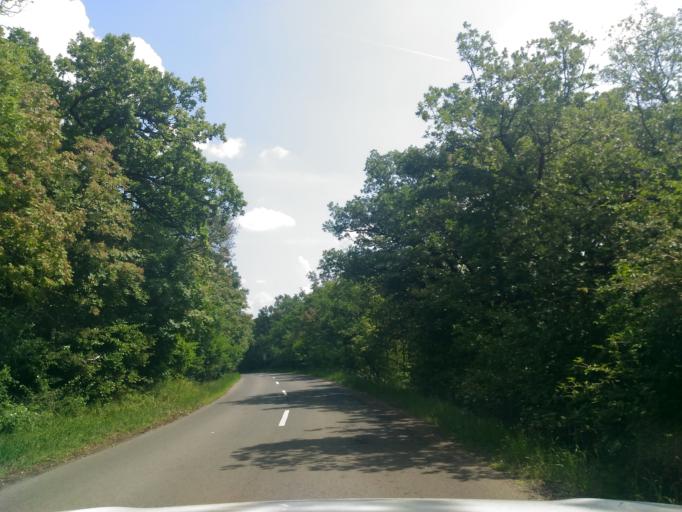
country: HU
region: Baranya
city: Pecs
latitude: 46.0980
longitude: 18.2238
